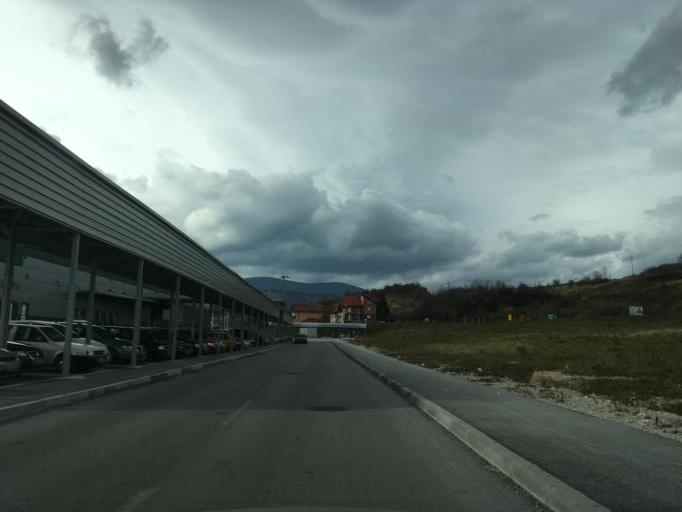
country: BA
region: Federation of Bosnia and Herzegovina
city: Bugojno
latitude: 44.0546
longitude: 17.4371
